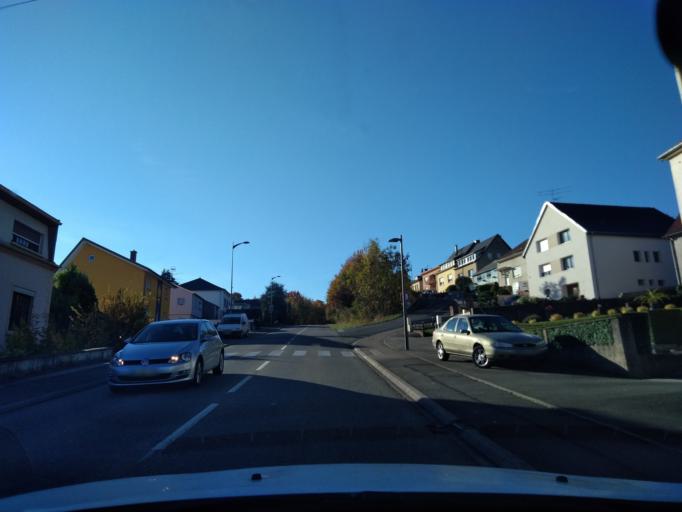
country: FR
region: Lorraine
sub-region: Departement de la Moselle
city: Remelfing
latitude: 49.0929
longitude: 7.0821
